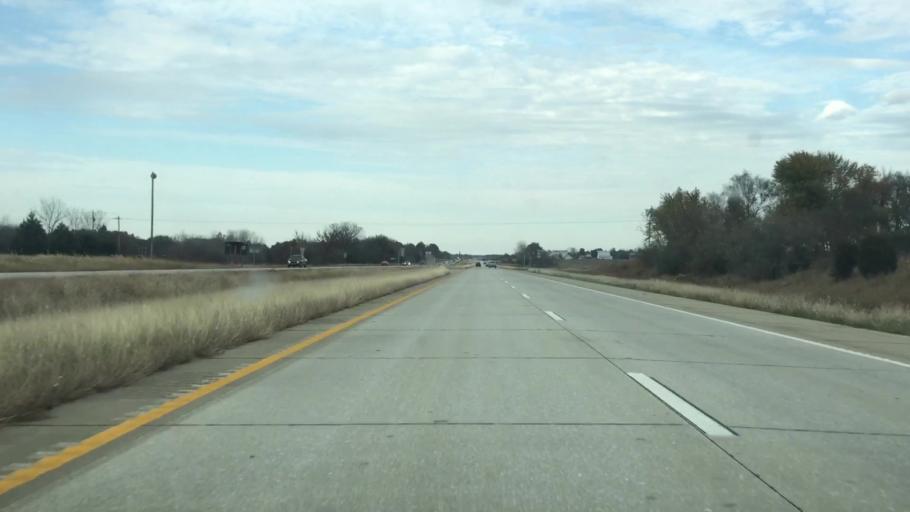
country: US
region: Missouri
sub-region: Henry County
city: Clinton
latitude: 38.2993
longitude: -93.7587
